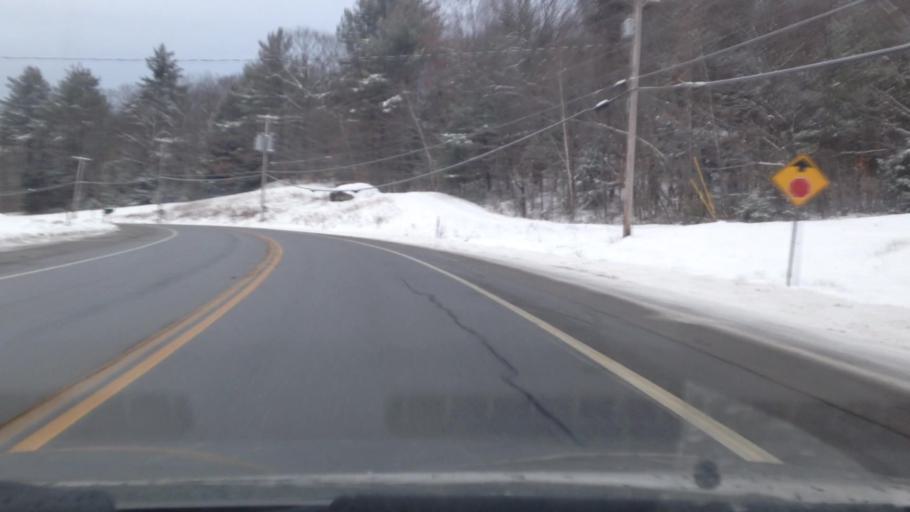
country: US
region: New Hampshire
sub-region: Cheshire County
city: Keene
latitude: 42.9695
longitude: -72.2616
